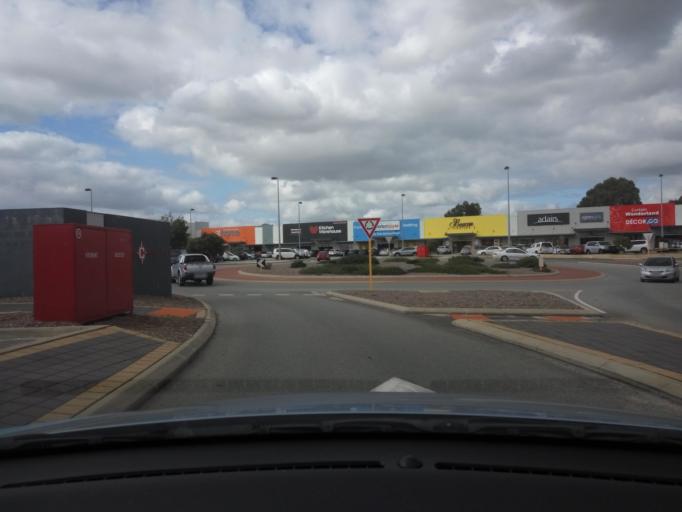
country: AU
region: Western Australia
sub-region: City of Cockburn
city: Success
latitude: -32.1256
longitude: 115.8697
